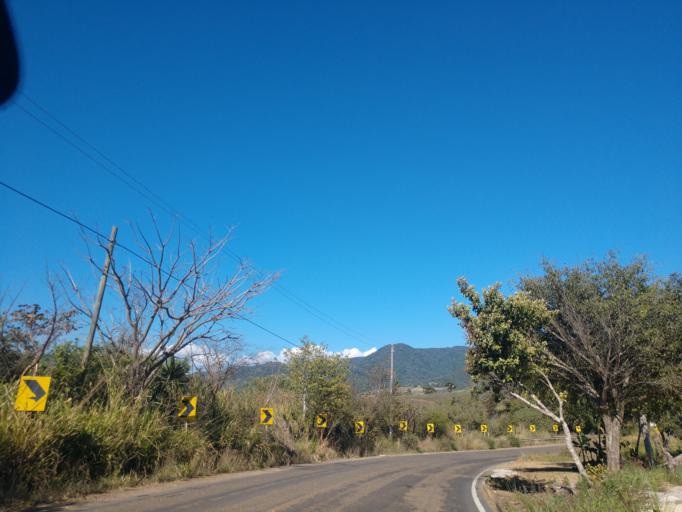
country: MX
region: Nayarit
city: Compostela
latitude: 21.2713
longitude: -104.8908
